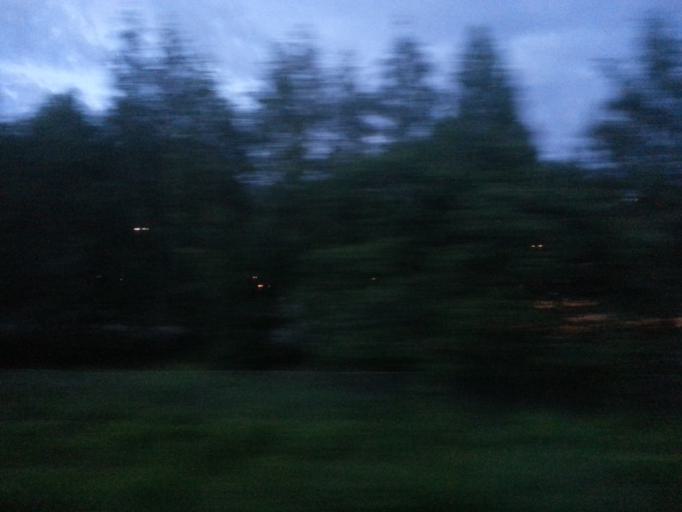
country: NO
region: Akershus
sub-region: Skedsmo
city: Lillestrom
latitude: 59.9621
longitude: 11.0649
